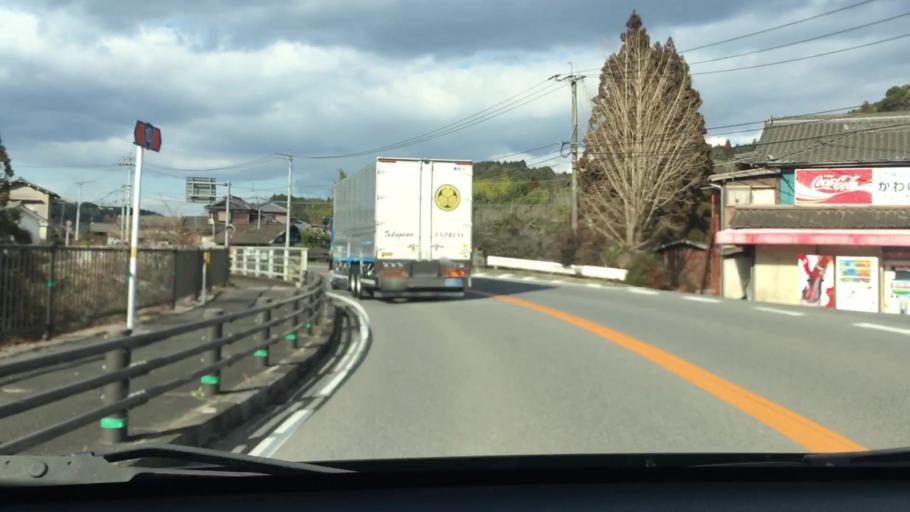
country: JP
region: Oita
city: Usuki
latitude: 33.0172
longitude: 131.7010
